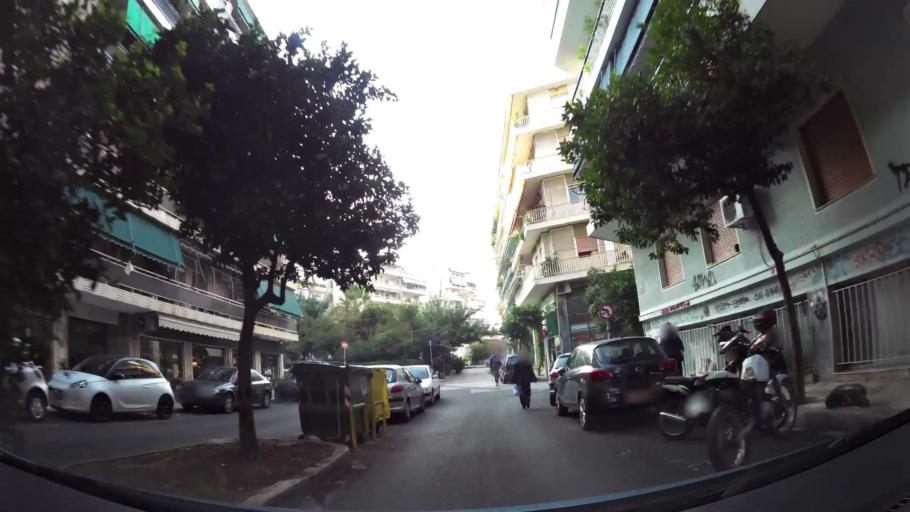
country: GR
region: Attica
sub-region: Nomarchia Athinas
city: Kaisariani
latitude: 37.9771
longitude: 23.7613
